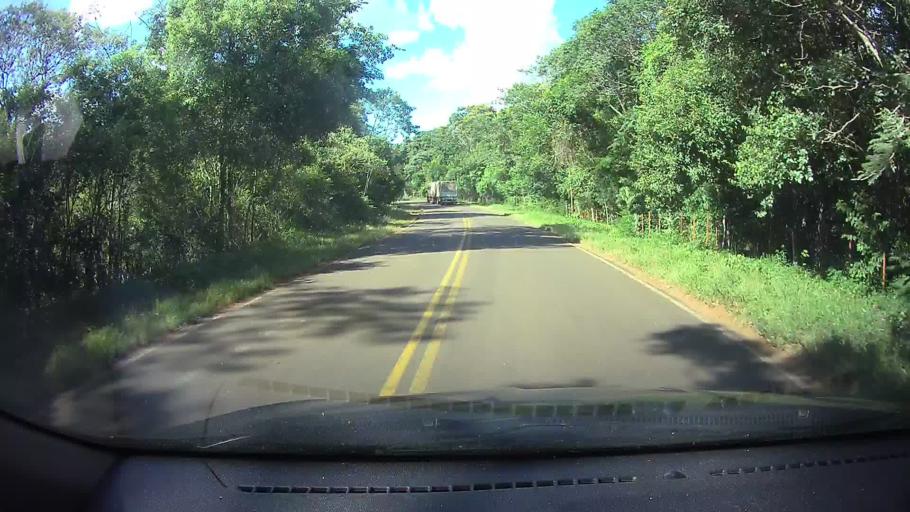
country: PY
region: Paraguari
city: Sapucai
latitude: -25.6679
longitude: -56.8580
